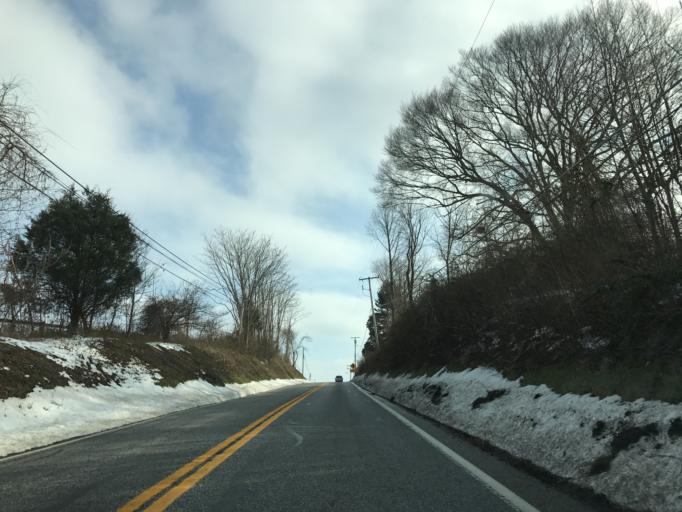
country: US
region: Maryland
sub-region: Harford County
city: South Bel Air
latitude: 39.5884
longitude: -76.2590
